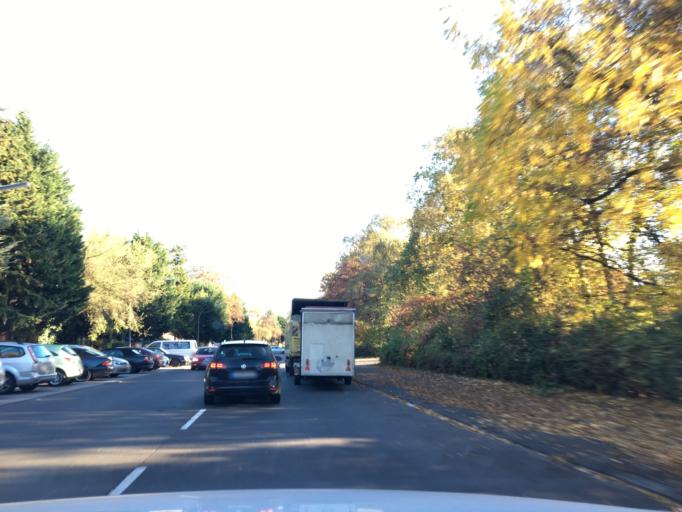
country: DE
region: North Rhine-Westphalia
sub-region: Regierungsbezirk Koln
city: Bilderstoeckchen
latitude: 50.9710
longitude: 6.9255
